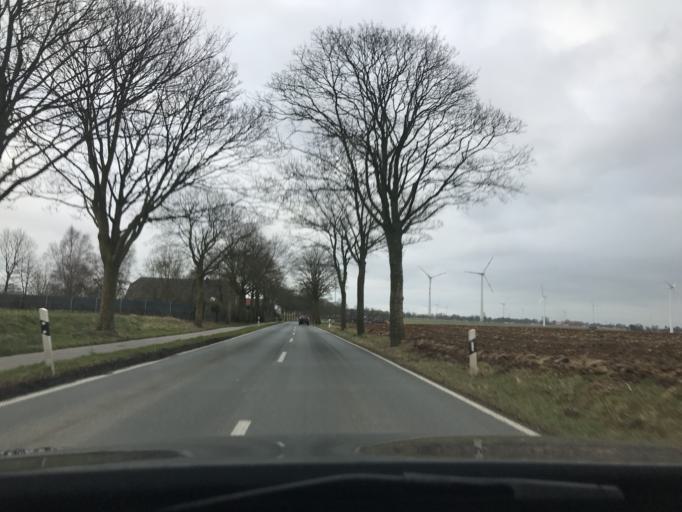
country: DE
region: North Rhine-Westphalia
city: Kalkar
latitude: 51.7192
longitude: 6.2210
